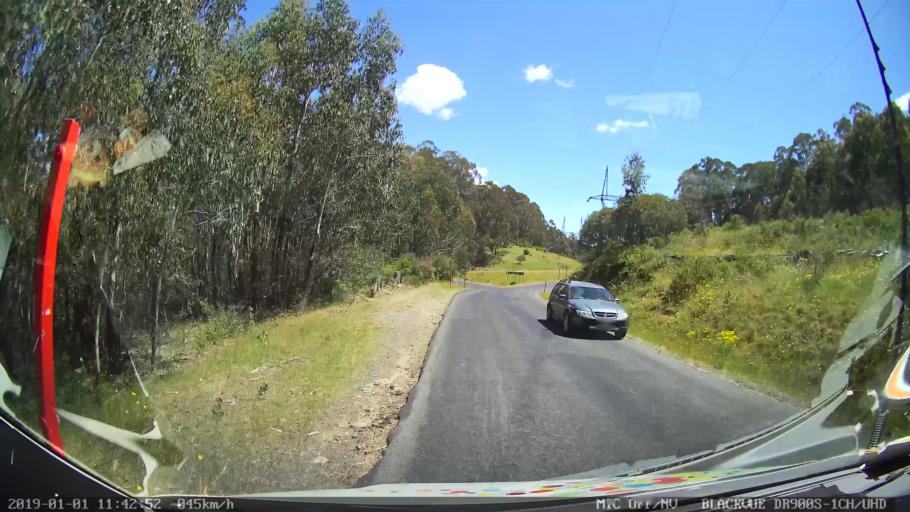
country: AU
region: New South Wales
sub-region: Snowy River
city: Jindabyne
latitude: -35.9066
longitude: 148.3837
